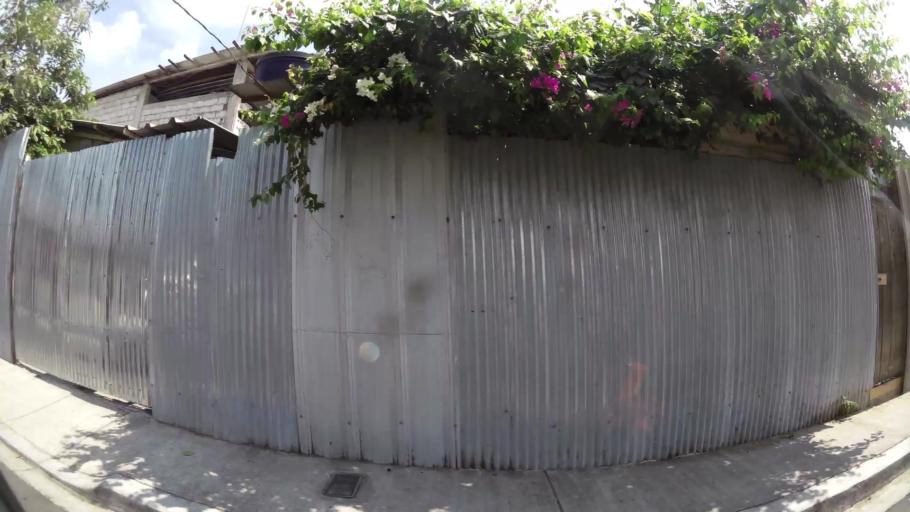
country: EC
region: Guayas
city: Guayaquil
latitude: -2.2633
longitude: -79.8717
